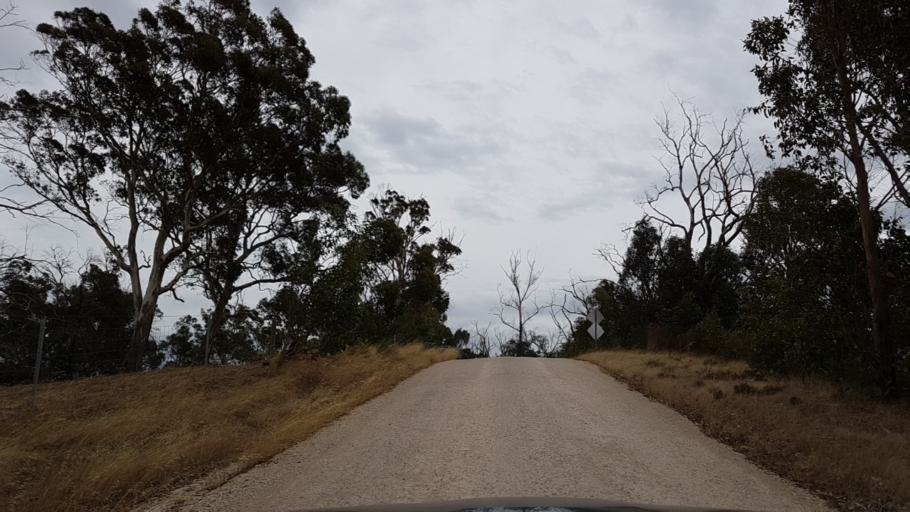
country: AU
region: South Australia
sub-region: Tea Tree Gully
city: Golden Grove
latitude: -34.7886
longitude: 138.8127
